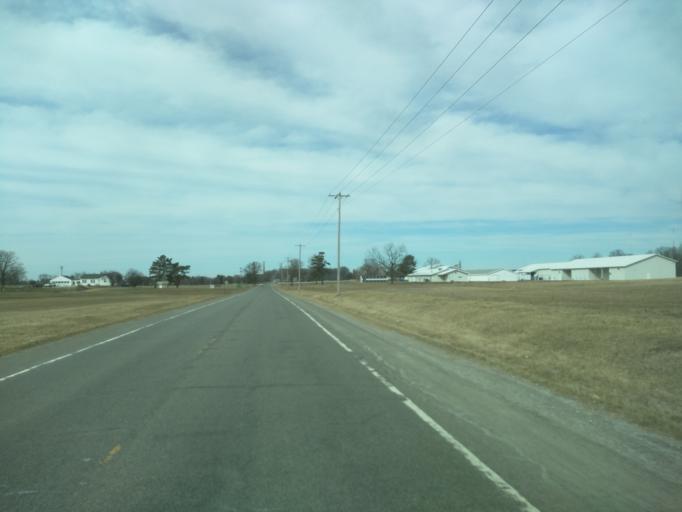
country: US
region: Michigan
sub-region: Ingham County
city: East Lansing
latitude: 42.6973
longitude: -84.4840
